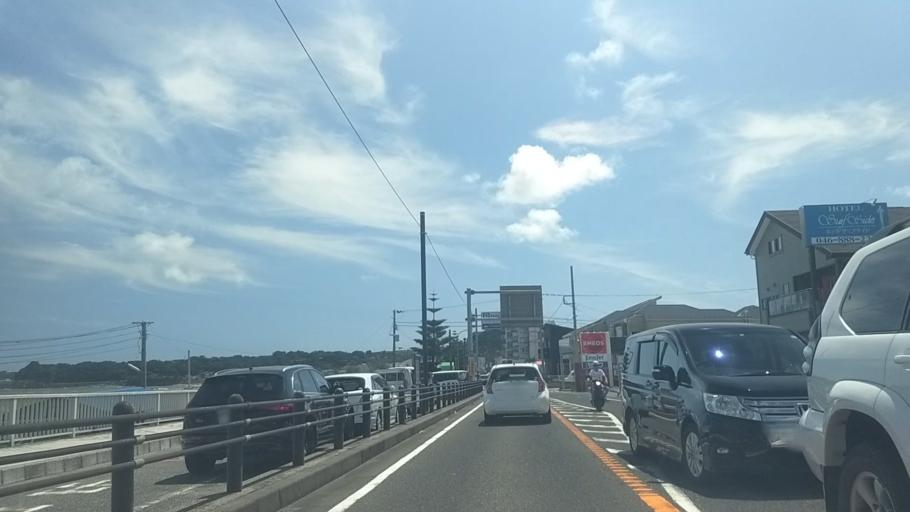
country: JP
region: Kanagawa
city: Miura
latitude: 35.1847
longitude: 139.6552
